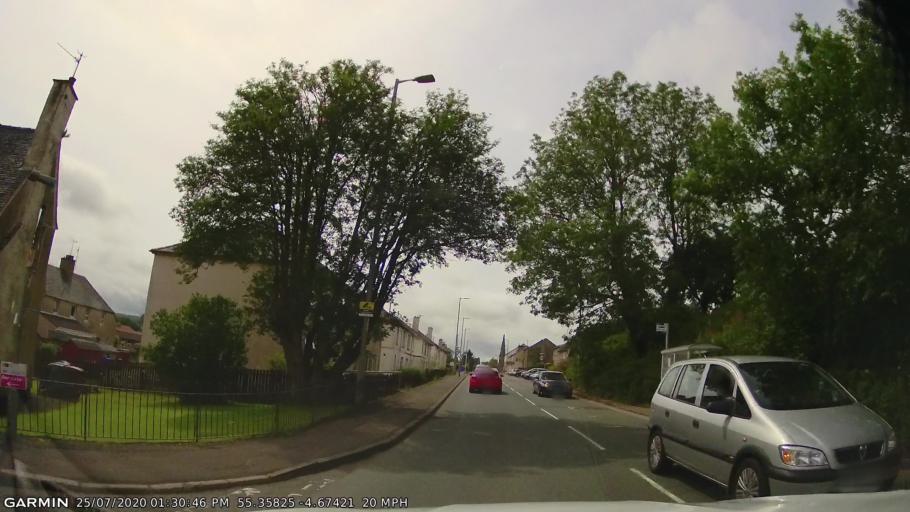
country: GB
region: Scotland
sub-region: South Ayrshire
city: Maybole
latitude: 55.3582
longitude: -4.6742
